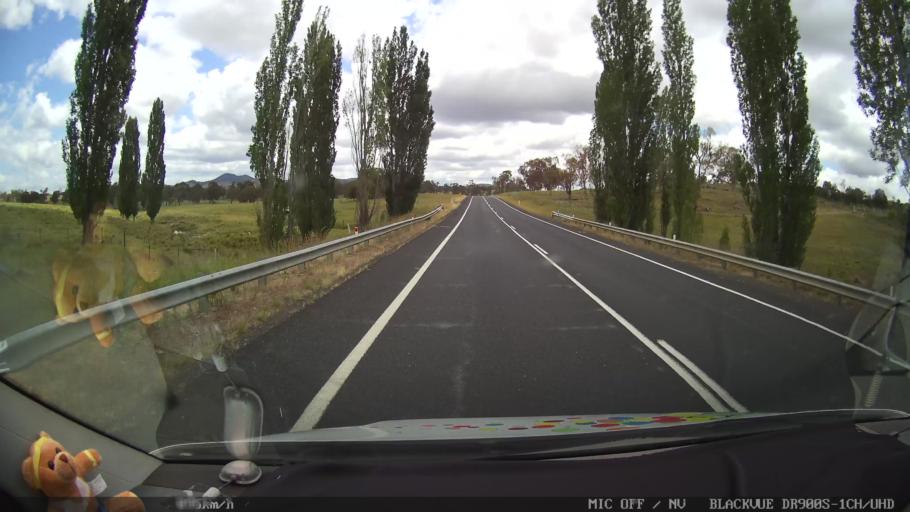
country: AU
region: New South Wales
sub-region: Glen Innes Severn
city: Glen Innes
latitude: -29.3894
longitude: 151.8867
